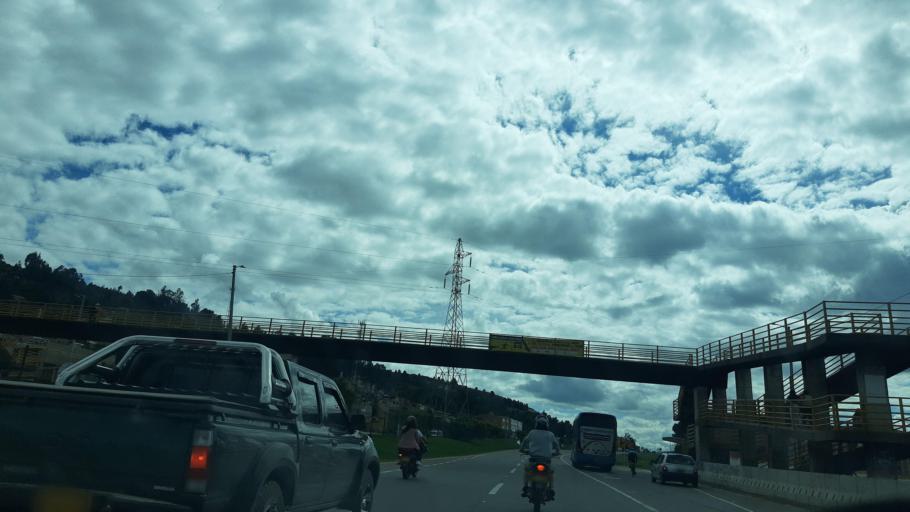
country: CO
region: Cundinamarca
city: Tocancipa
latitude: 4.9630
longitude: -73.9099
